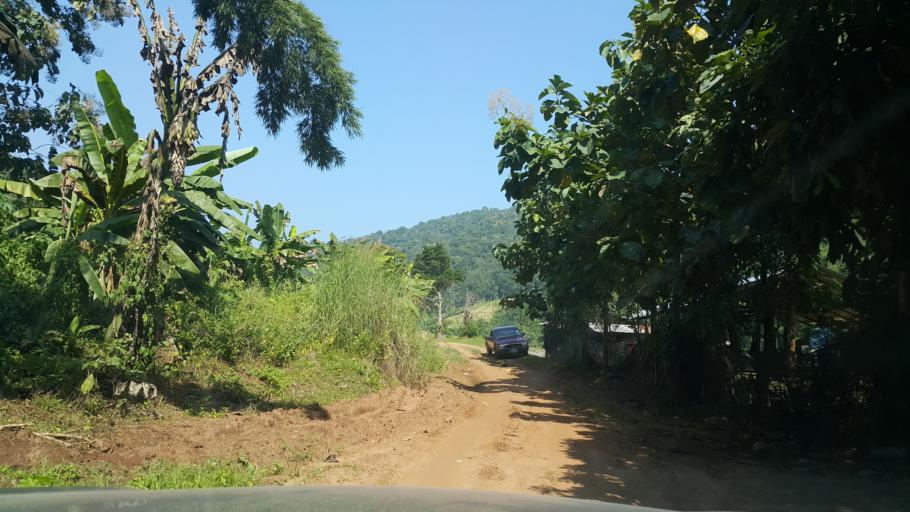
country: TH
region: Chiang Mai
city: Samoeng
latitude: 18.9425
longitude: 98.6200
